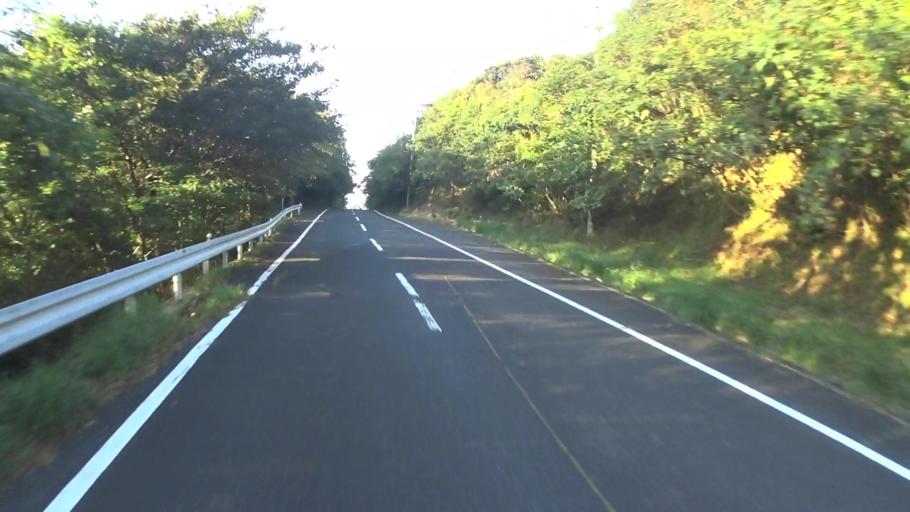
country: JP
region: Hyogo
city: Toyooka
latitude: 35.6884
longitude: 134.9874
